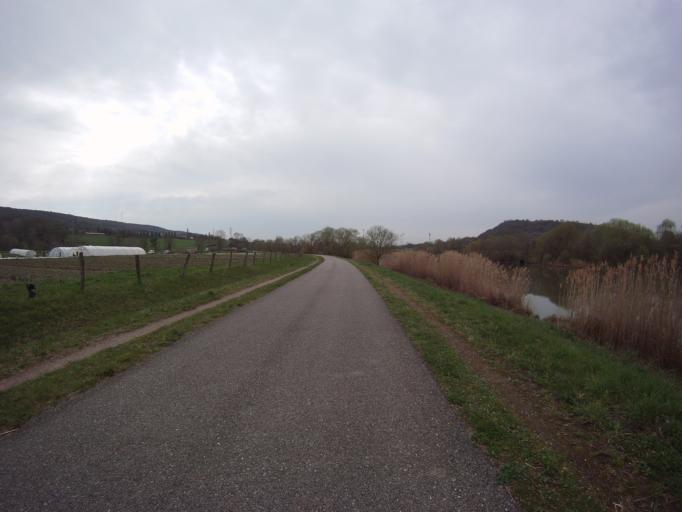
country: FR
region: Lorraine
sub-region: Departement de Meurthe-et-Moselle
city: Champigneulles
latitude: 48.7342
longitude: 6.1722
